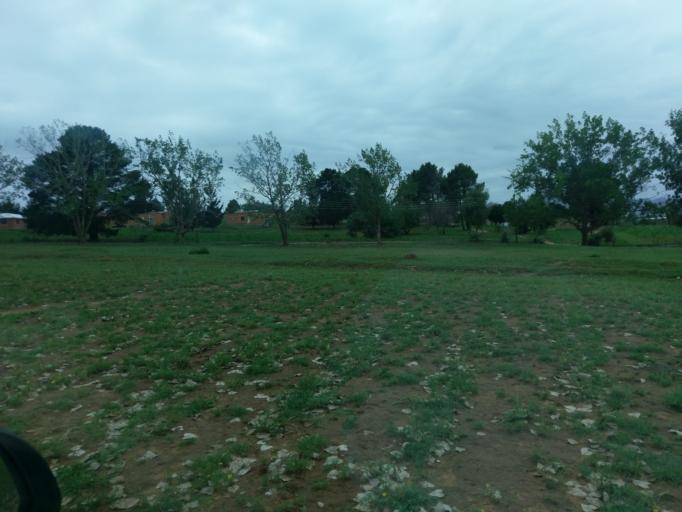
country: LS
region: Berea
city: Teyateyaneng
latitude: -29.1069
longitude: 27.9618
